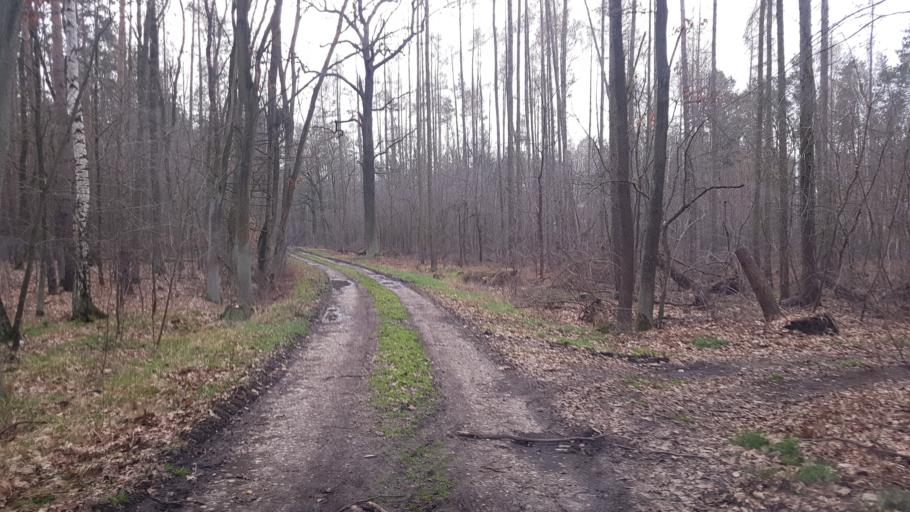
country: DE
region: Brandenburg
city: Falkenberg
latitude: 51.5837
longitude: 13.3022
